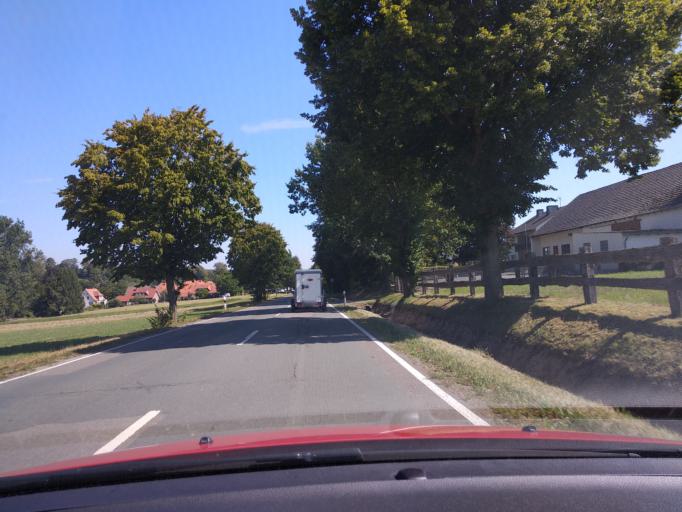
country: DE
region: North Rhine-Westphalia
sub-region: Regierungsbezirk Detmold
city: Willebadessen
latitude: 51.6554
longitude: 9.1107
